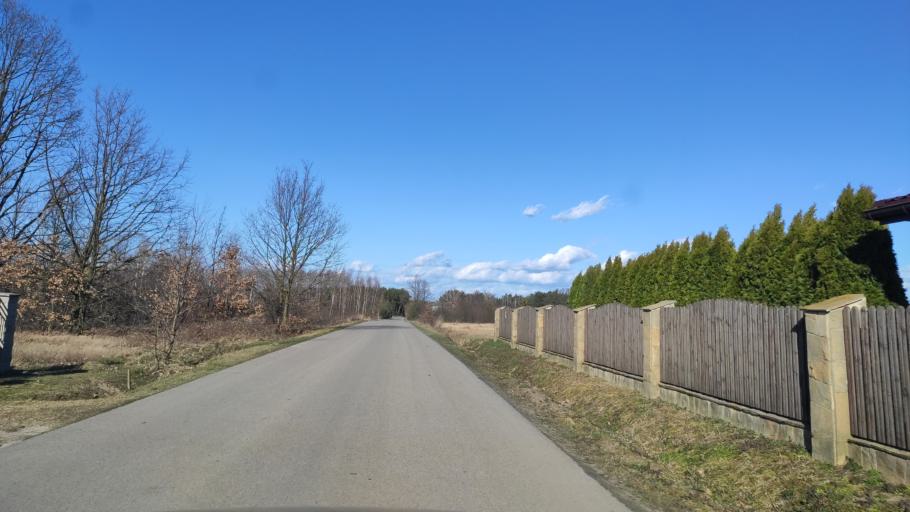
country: PL
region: Masovian Voivodeship
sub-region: Powiat radomski
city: Jastrzebia
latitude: 51.4558
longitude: 21.2584
